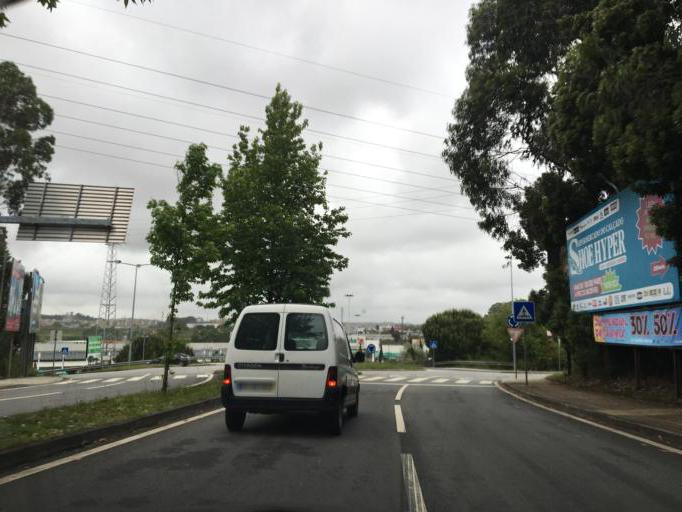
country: PT
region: Porto
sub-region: Maia
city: Maia
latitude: 41.2467
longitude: -8.6231
